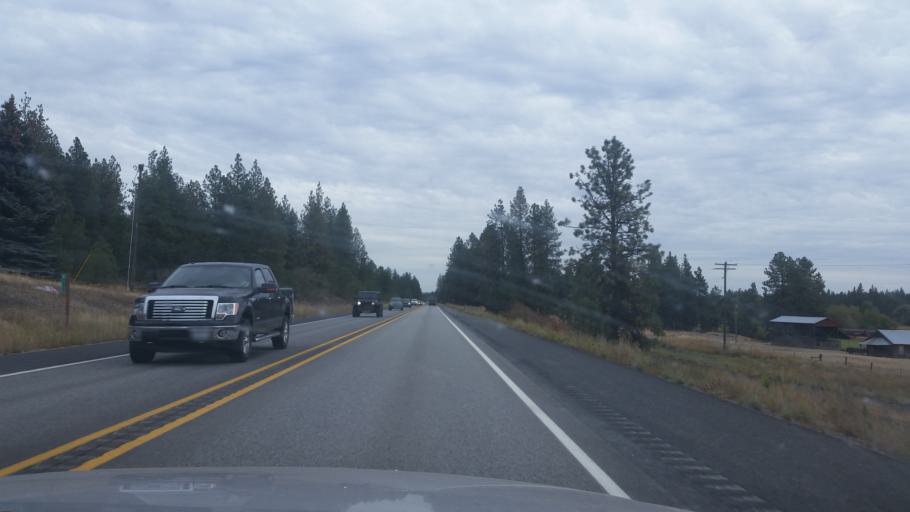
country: US
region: Washington
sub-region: Spokane County
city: Cheney
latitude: 47.5408
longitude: -117.5803
